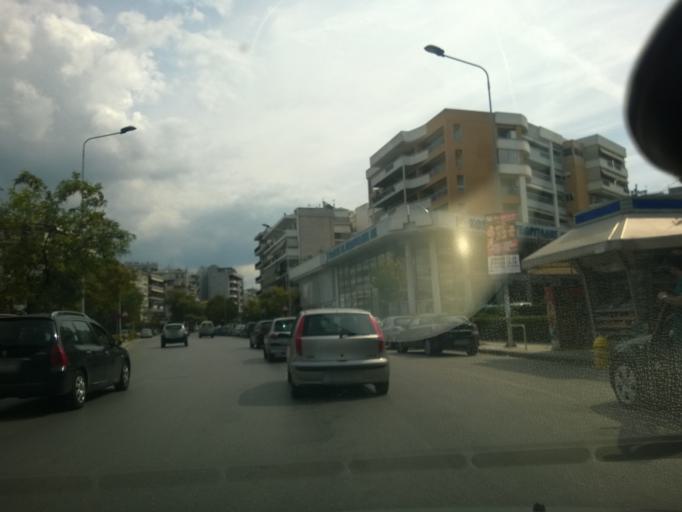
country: GR
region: Central Macedonia
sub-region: Nomos Thessalonikis
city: Kalamaria
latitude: 40.5840
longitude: 22.9589
